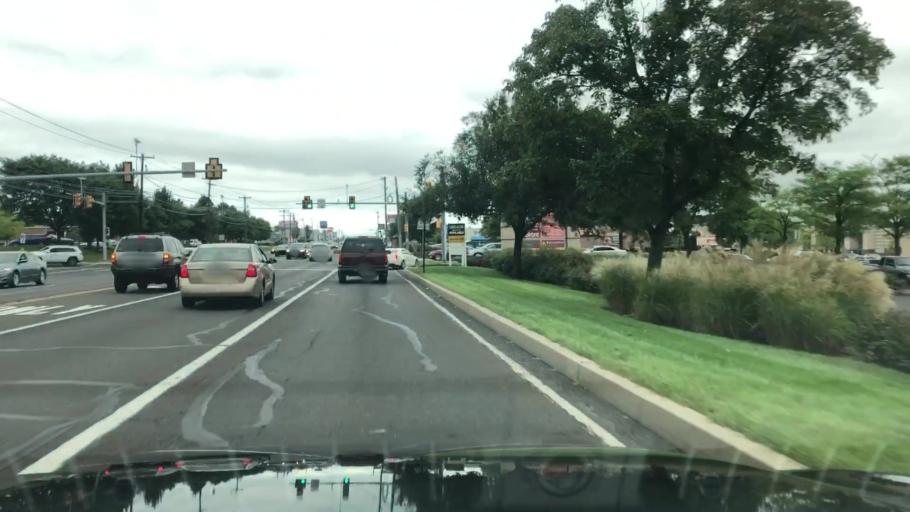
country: US
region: Pennsylvania
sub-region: Bucks County
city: Langhorne Manor
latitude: 40.1692
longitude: -74.8944
